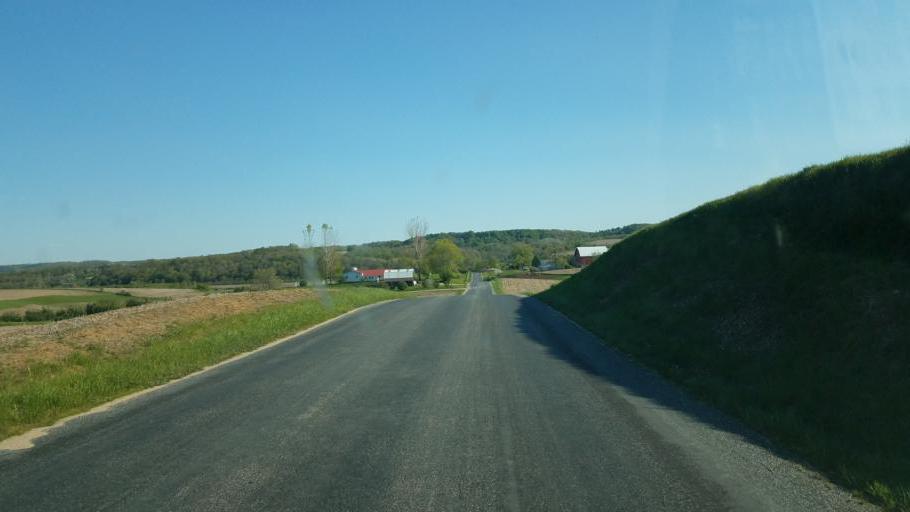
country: US
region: Wisconsin
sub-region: Vernon County
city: Hillsboro
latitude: 43.6670
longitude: -90.3776
